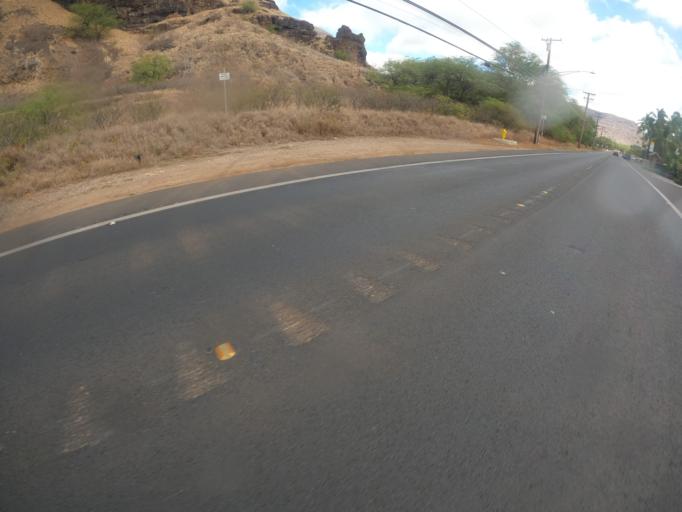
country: US
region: Hawaii
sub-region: Honolulu County
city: Makaha
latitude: 21.4796
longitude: -158.2244
